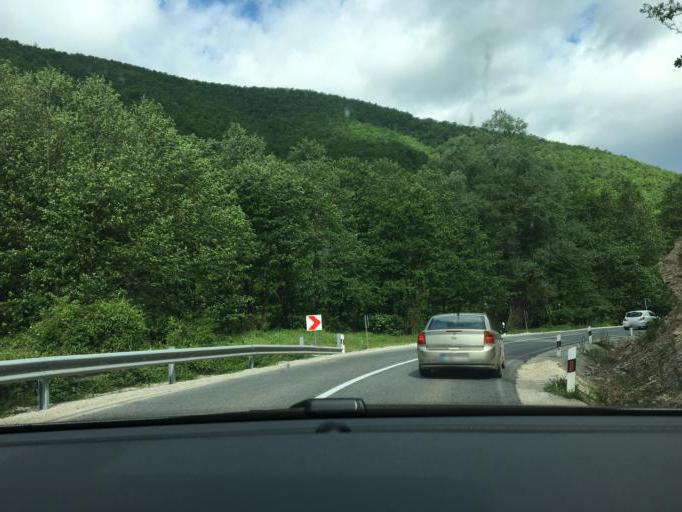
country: MK
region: Resen
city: Jankovec
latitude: 41.1397
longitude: 21.0015
